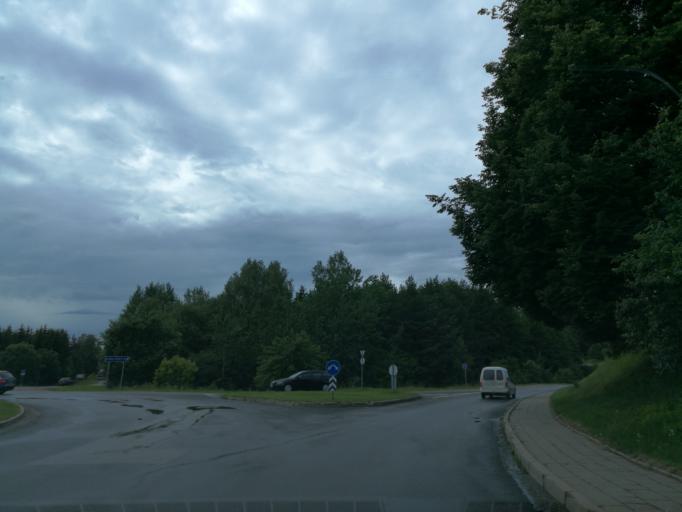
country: LT
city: Trakai
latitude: 54.6533
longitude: 24.9181
